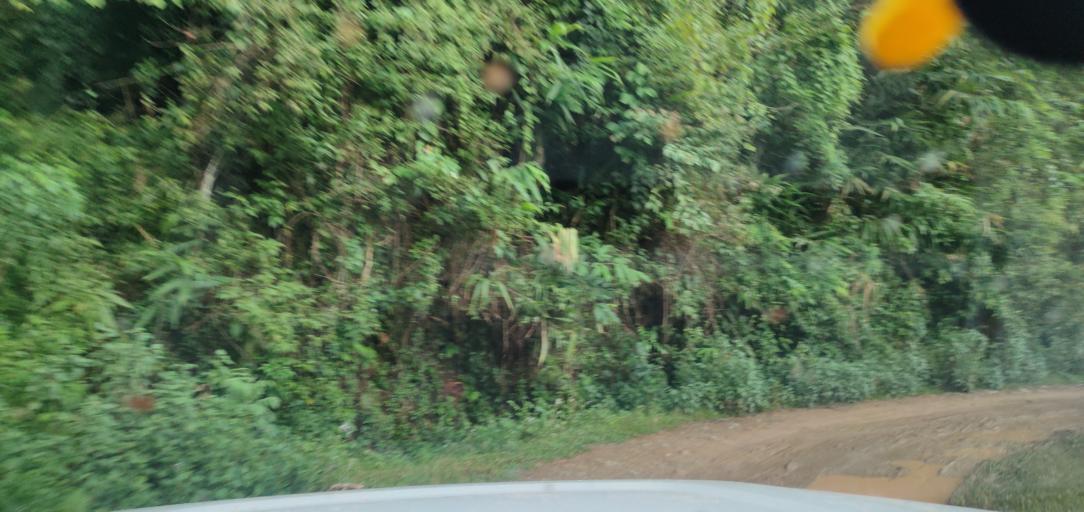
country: LA
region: Phongsali
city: Phongsali
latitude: 21.4463
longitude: 102.2930
